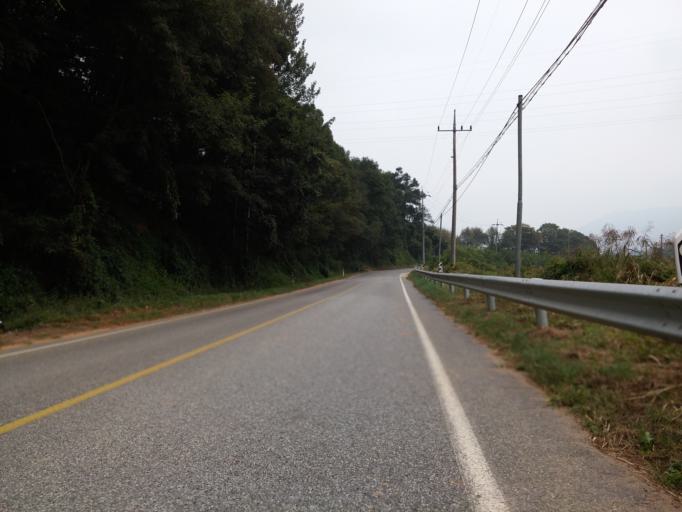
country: KR
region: Chungcheongbuk-do
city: Okcheon
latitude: 36.3934
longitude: 127.7035
